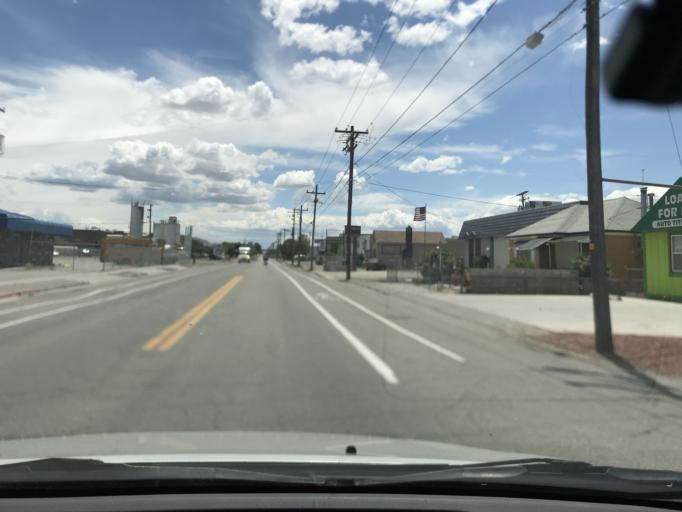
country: US
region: Utah
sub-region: Salt Lake County
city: Centerfield
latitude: 40.6977
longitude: -111.8998
